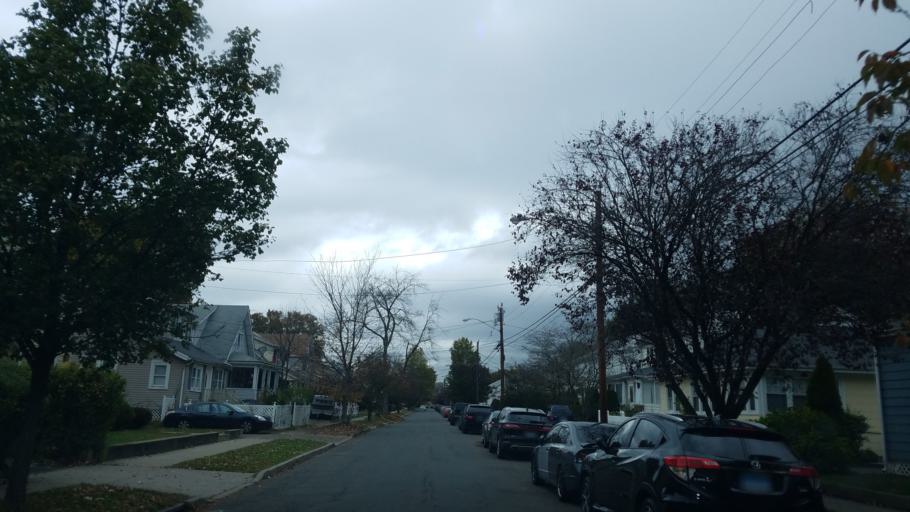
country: US
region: Connecticut
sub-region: Fairfield County
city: Stamford
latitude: 41.0594
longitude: -73.5230
